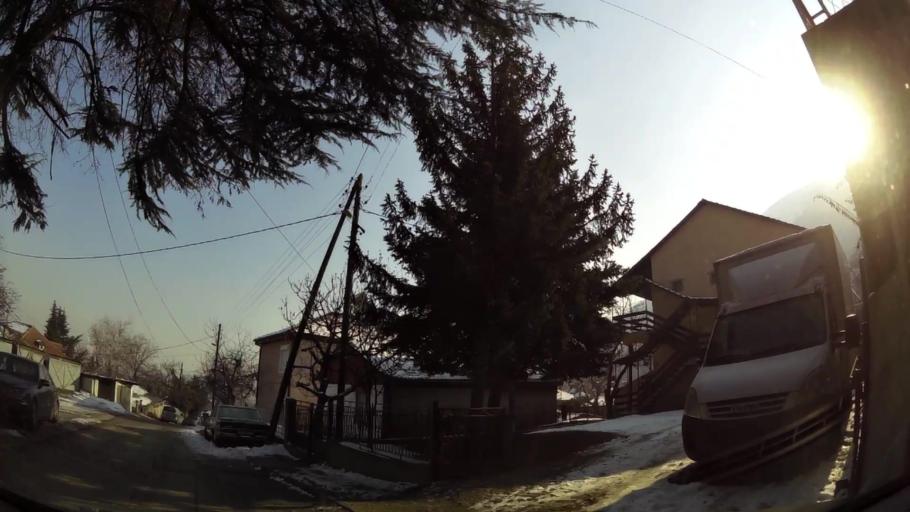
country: MK
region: Sopiste
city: Sopishte
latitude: 41.9736
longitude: 21.4343
